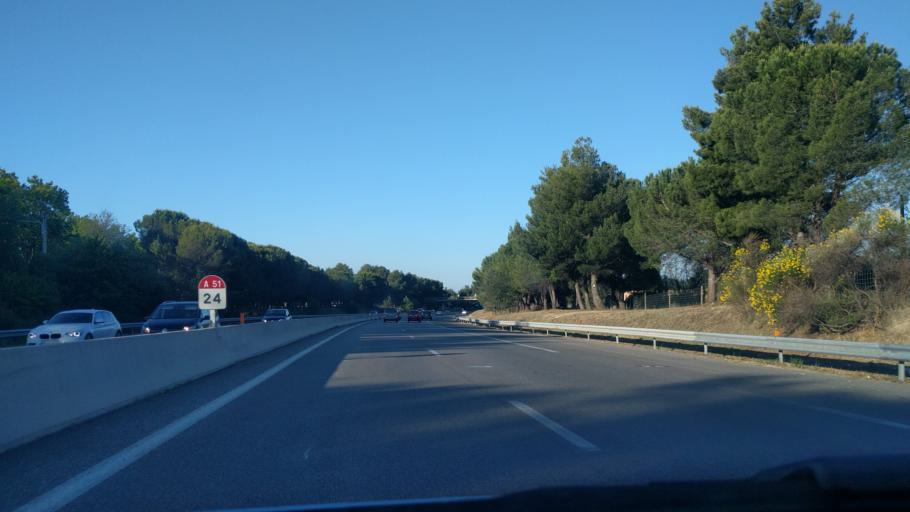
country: FR
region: Provence-Alpes-Cote d'Azur
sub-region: Departement des Bouches-du-Rhone
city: Venelles
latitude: 43.5672
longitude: 5.4650
